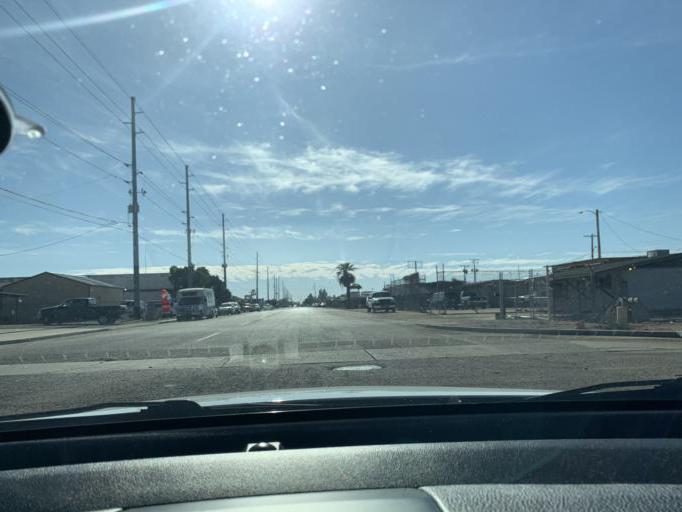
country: US
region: Arizona
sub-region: Maricopa County
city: Peoria
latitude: 33.6875
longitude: -112.1086
